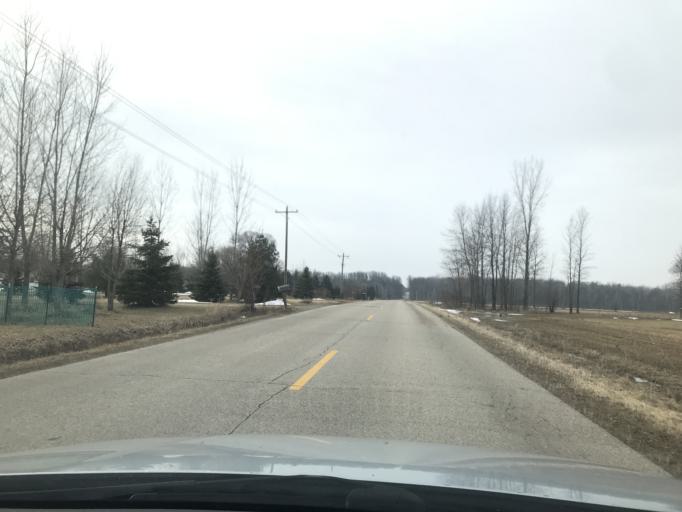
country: US
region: Wisconsin
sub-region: Oconto County
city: Oconto Falls
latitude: 44.8411
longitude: -88.1678
